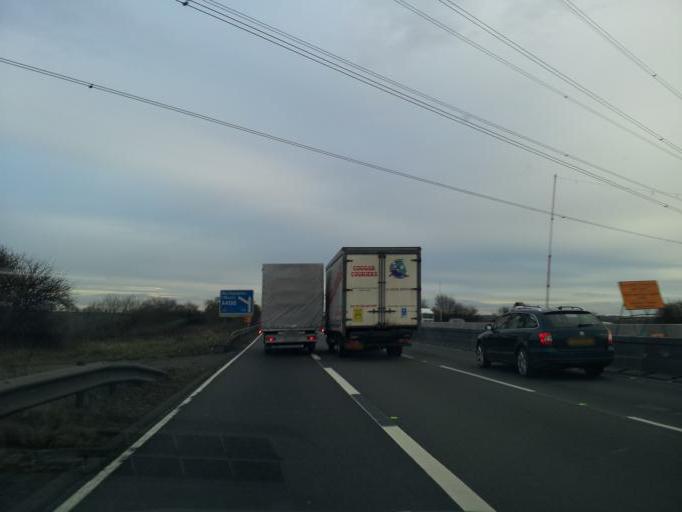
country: GB
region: England
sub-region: Northamptonshire
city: Bugbrooke
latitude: 52.2390
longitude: -1.0450
